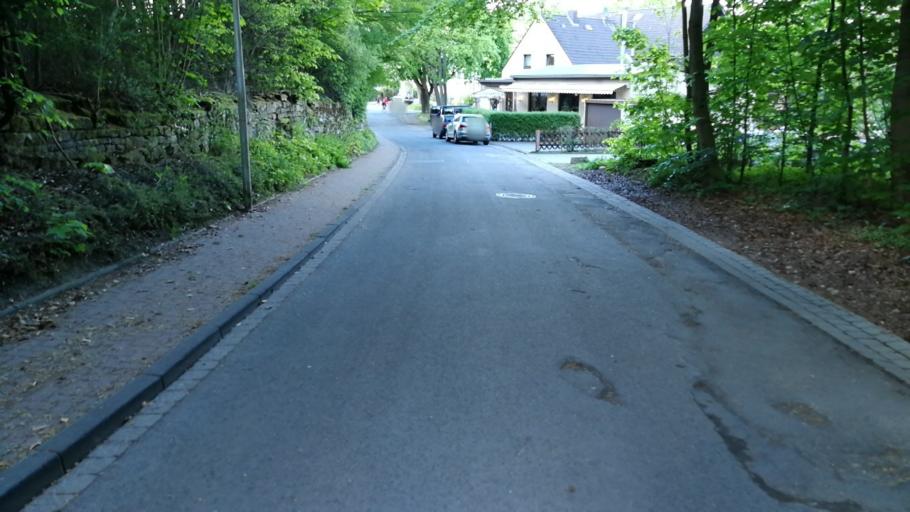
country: DE
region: Lower Saxony
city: Gehrden
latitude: 52.3121
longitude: 9.5915
